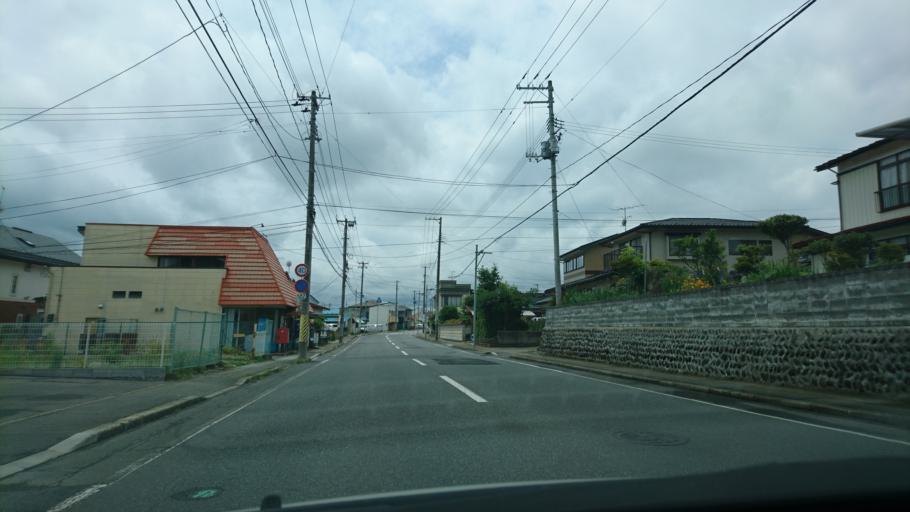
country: JP
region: Iwate
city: Ichinoseki
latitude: 38.9278
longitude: 141.1230
